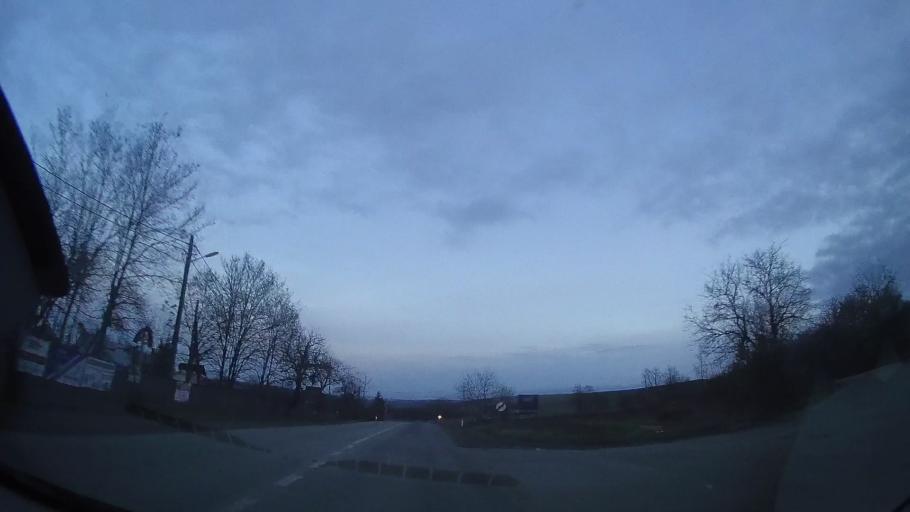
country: RO
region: Cluj
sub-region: Comuna Mociu
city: Mociu
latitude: 46.7982
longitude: 23.9996
